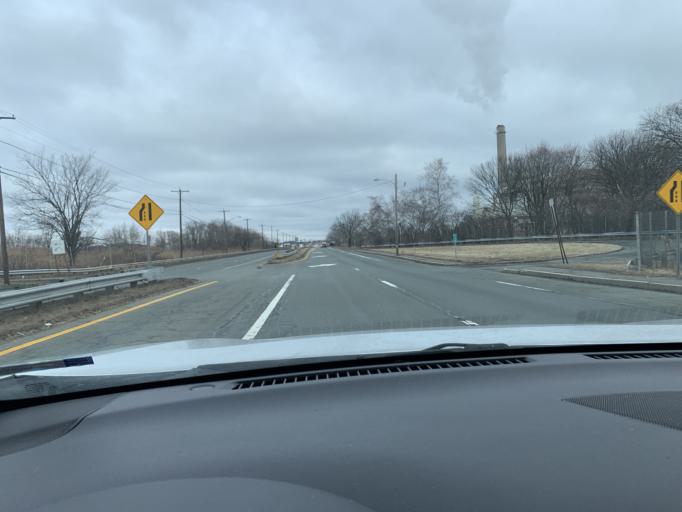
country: US
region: Massachusetts
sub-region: Essex County
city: Saugus
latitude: 42.4455
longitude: -70.9847
